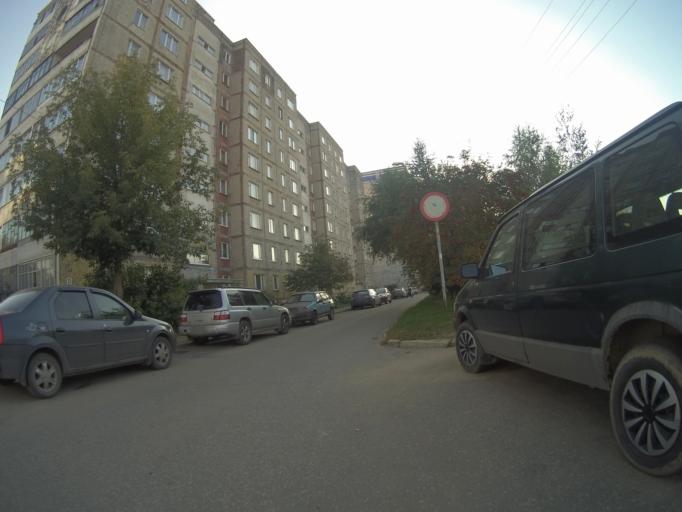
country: RU
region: Vladimir
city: Vladimir
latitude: 56.1091
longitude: 40.3480
